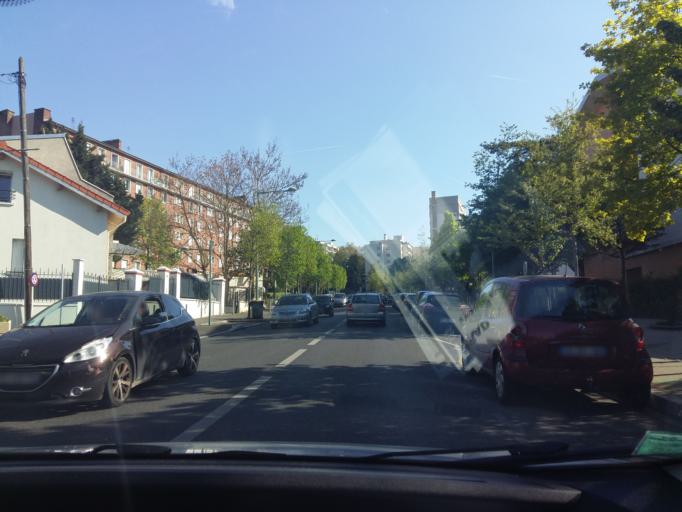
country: FR
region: Ile-de-France
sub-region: Departement du Val-de-Marne
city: Arcueil
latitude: 48.8040
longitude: 2.3380
